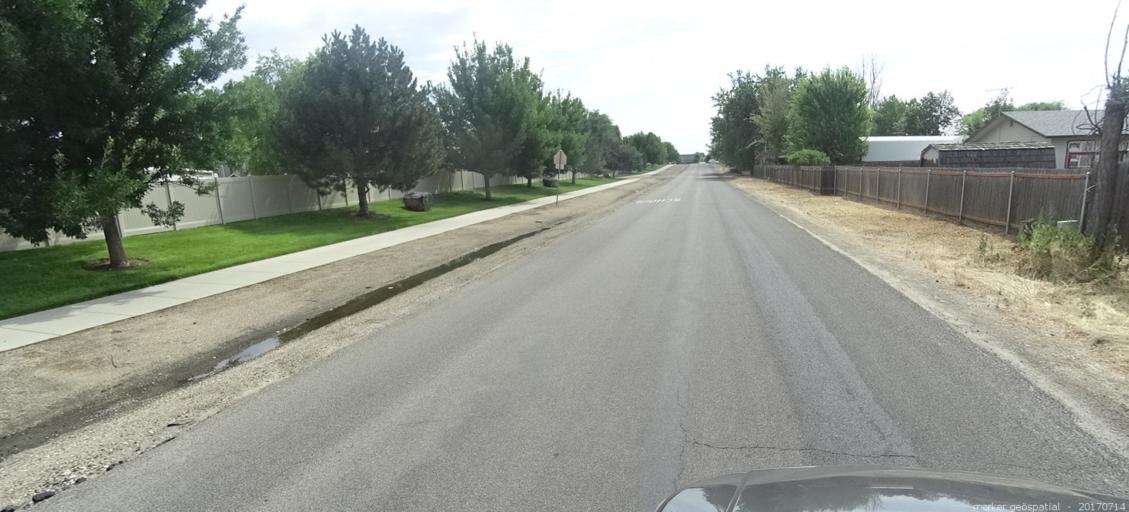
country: US
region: Idaho
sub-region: Ada County
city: Kuna
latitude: 43.4921
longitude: -116.4086
